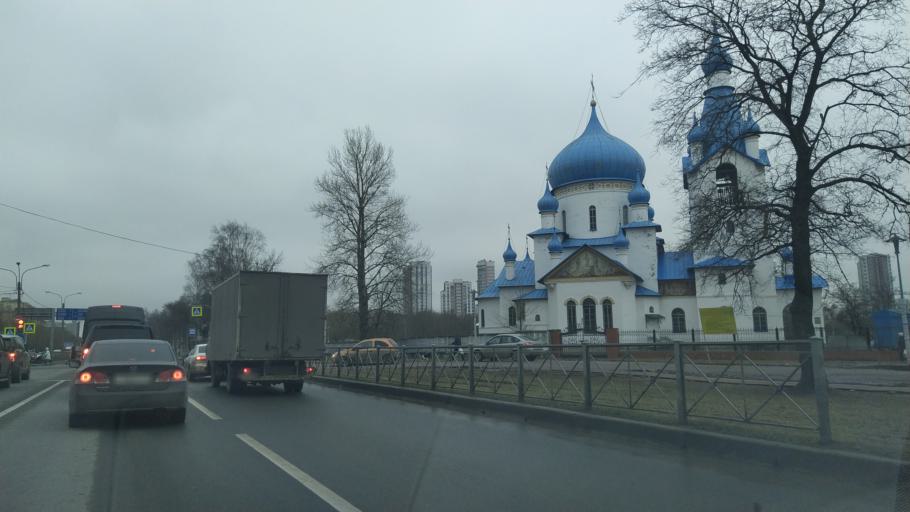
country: RU
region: St.-Petersburg
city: Kupchino
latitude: 59.8374
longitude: 30.3319
